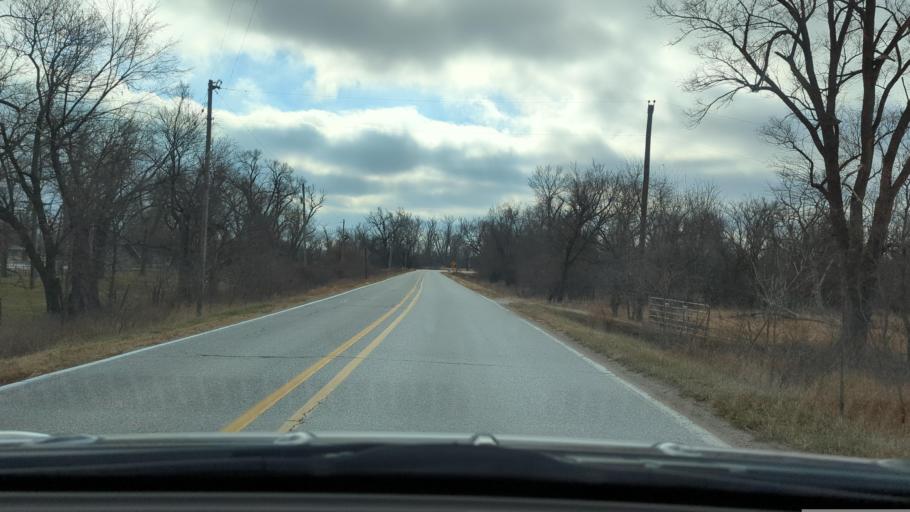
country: US
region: Nebraska
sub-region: Sarpy County
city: Offutt Air Force Base
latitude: 41.0671
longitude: -95.9232
